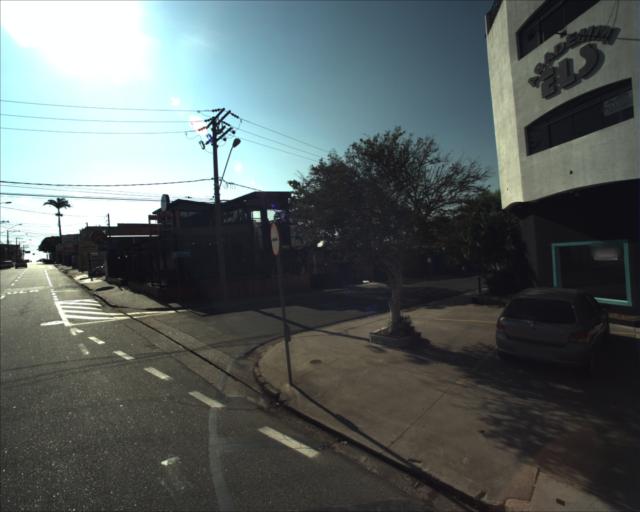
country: BR
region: Sao Paulo
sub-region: Sorocaba
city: Sorocaba
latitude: -23.4884
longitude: -47.4526
